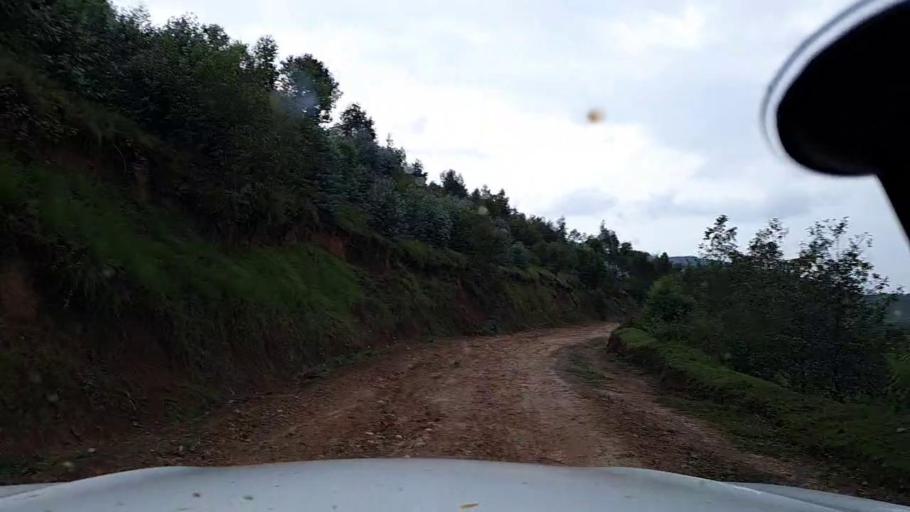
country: RW
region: Western Province
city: Kibuye
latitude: -2.0953
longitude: 29.4902
